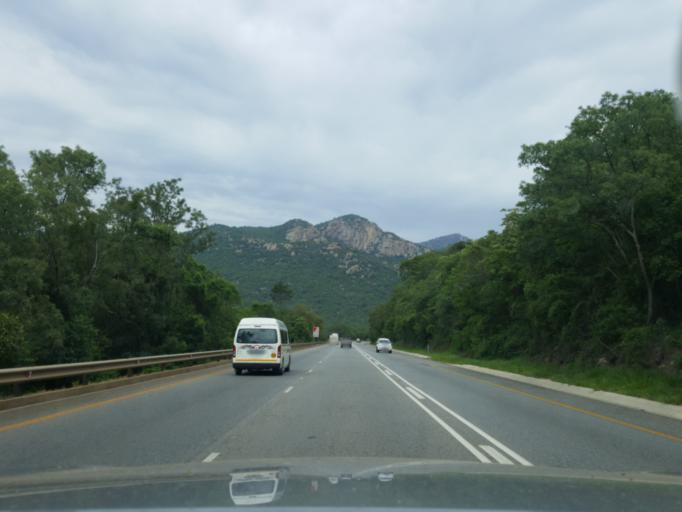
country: ZA
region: Mpumalanga
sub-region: Ehlanzeni District
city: Nelspruit
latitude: -25.5263
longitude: 31.2638
